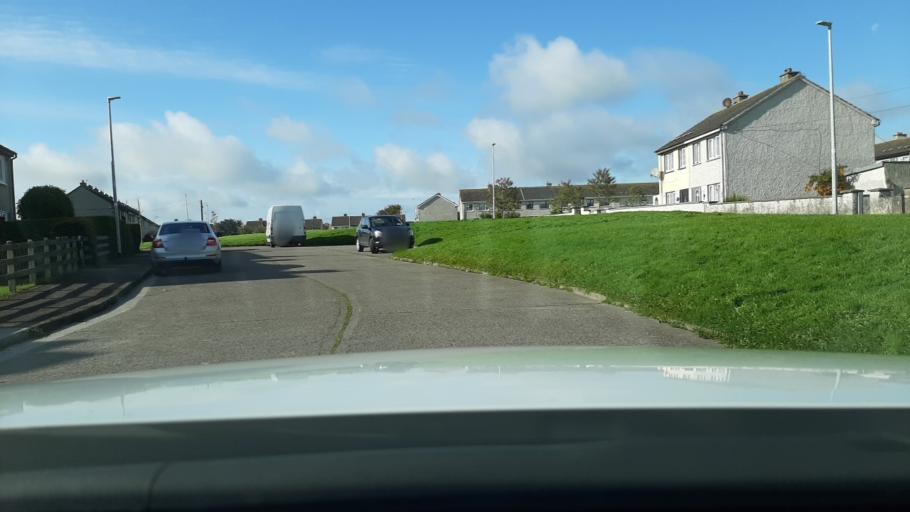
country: IE
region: Leinster
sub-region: Kildare
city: Kildare
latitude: 53.1624
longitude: -6.9020
